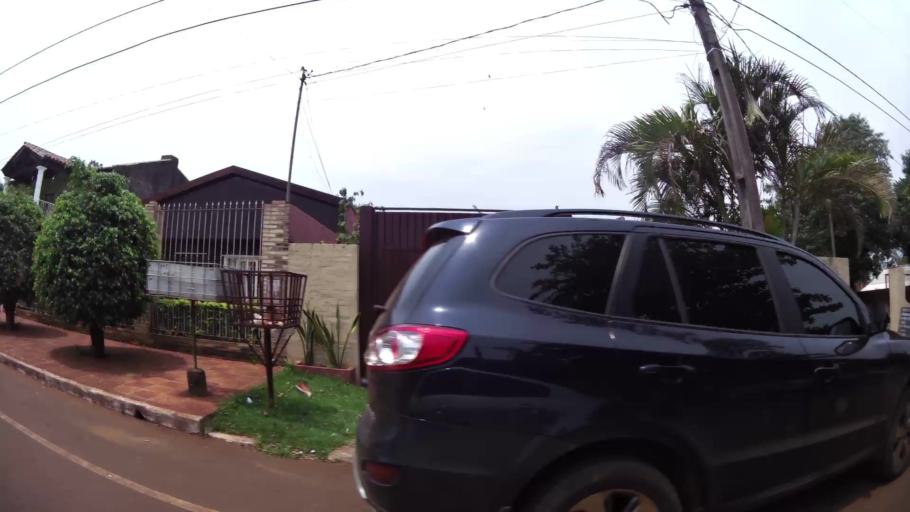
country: PY
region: Alto Parana
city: Presidente Franco
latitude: -25.5558
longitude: -54.6275
